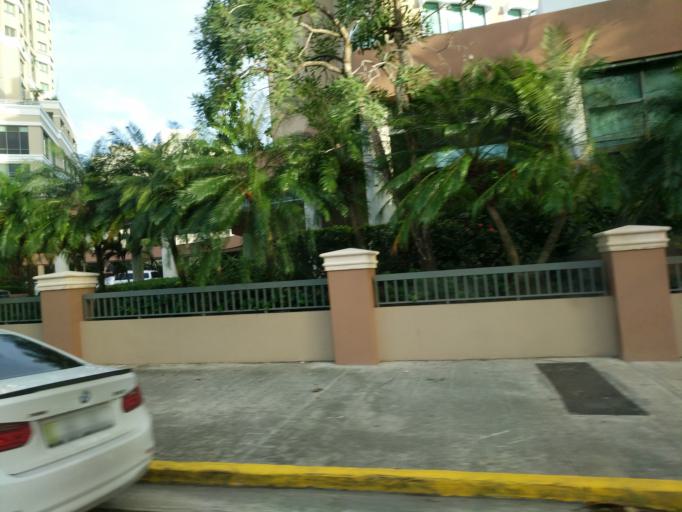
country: PR
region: San Juan
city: San Juan
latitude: 18.4513
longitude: -66.0646
